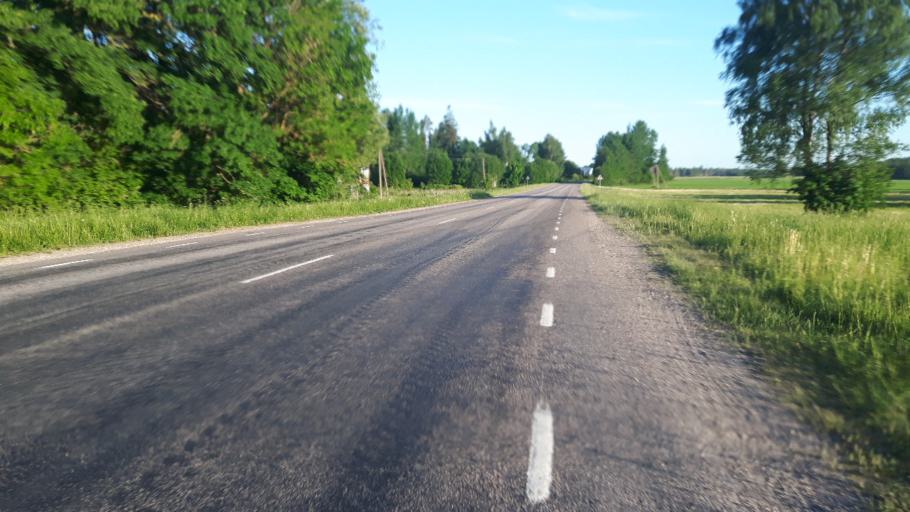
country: EE
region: Raplamaa
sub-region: Jaervakandi vald
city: Jarvakandi
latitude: 58.7974
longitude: 24.9277
